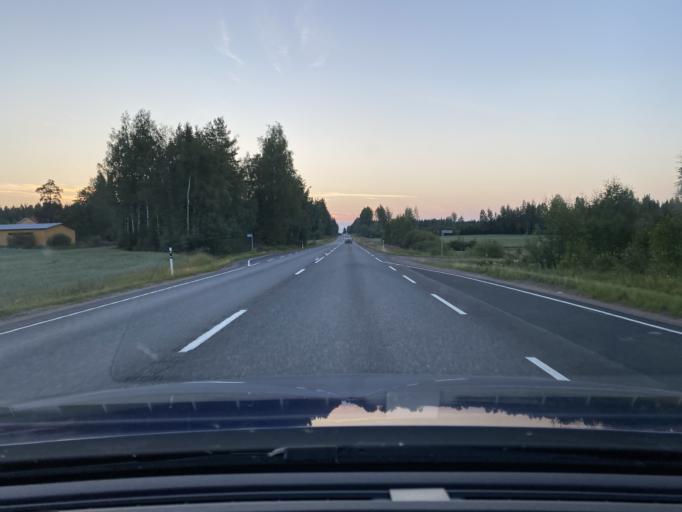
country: FI
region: Pirkanmaa
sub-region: Luoteis-Pirkanmaa
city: Ikaalinen
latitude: 61.8295
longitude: 22.9434
